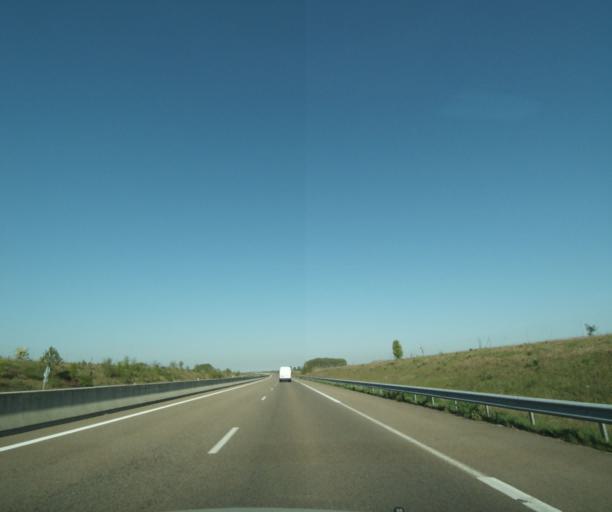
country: FR
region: Centre
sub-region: Departement du Loiret
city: Boynes
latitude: 48.1067
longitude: 2.3202
